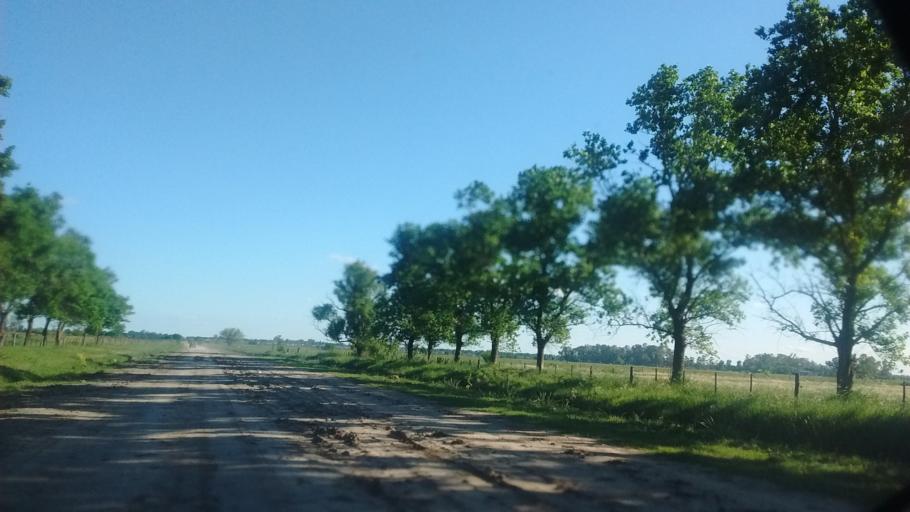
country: AR
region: Santa Fe
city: Funes
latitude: -32.8801
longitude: -60.7983
